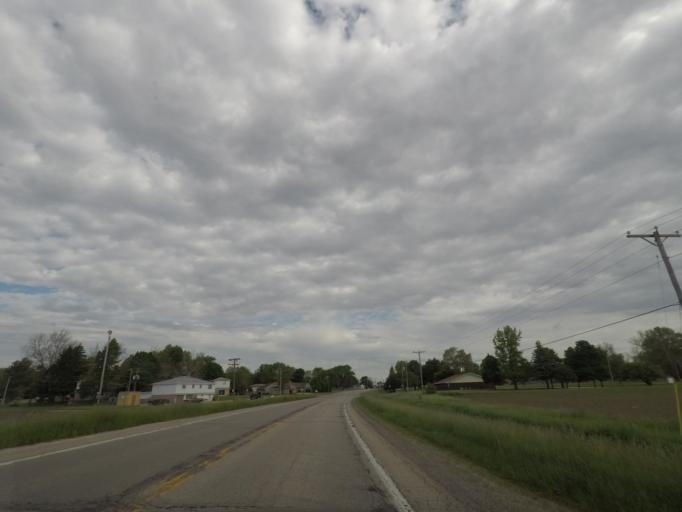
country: US
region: Illinois
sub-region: Logan County
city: Lincoln
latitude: 40.1350
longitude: -89.3479
